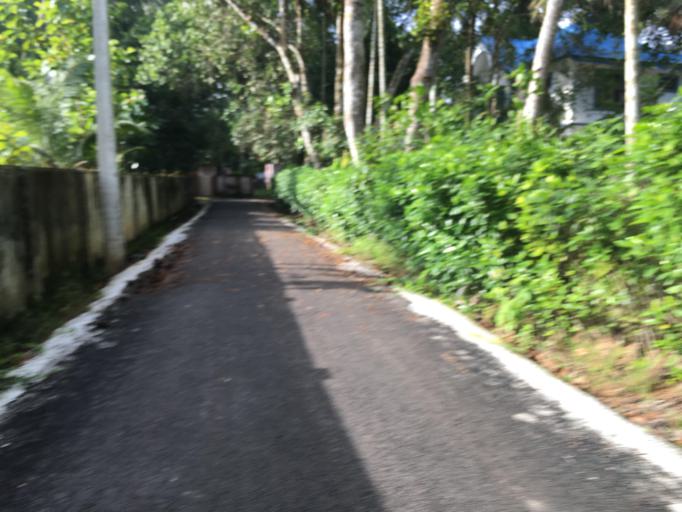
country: IN
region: Kerala
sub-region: Alappuzha
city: Kattanam
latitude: 9.1970
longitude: 76.5354
